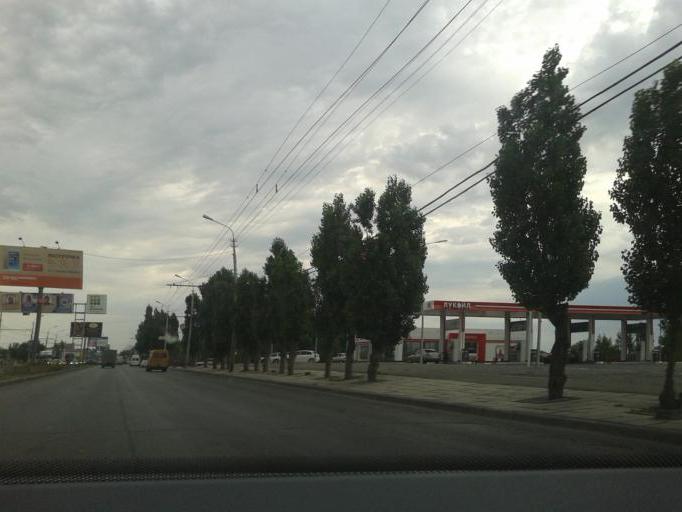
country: RU
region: Volgograd
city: Volgograd
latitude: 48.6242
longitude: 44.4259
